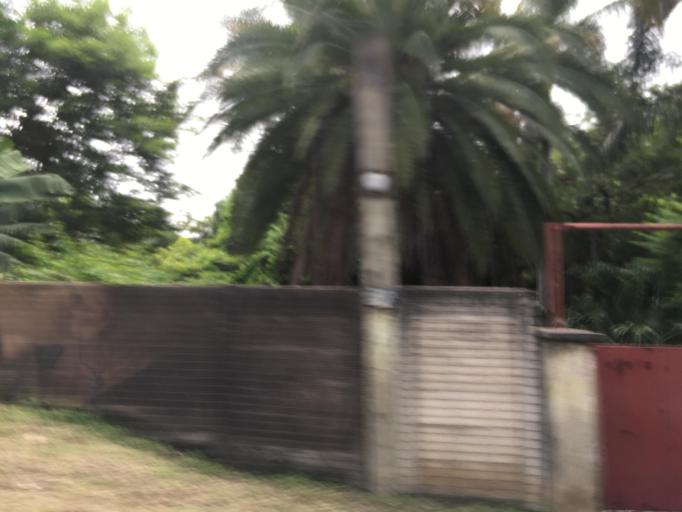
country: GT
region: Guatemala
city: Amatitlan
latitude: 14.4757
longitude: -90.6079
